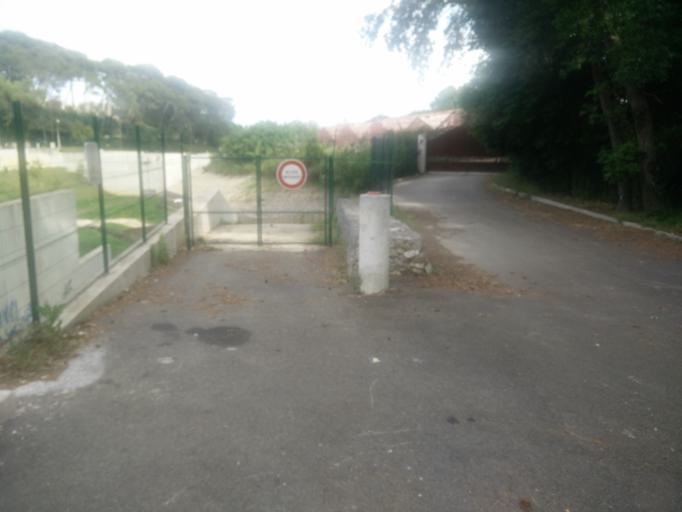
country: FR
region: Provence-Alpes-Cote d'Azur
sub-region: Departement des Alpes-Maritimes
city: Biot
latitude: 43.6008
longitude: 7.0972
